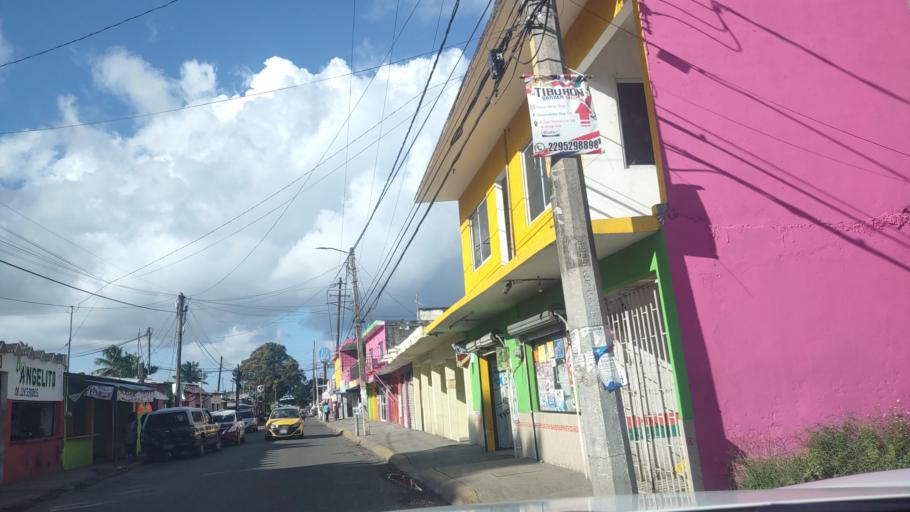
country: MX
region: Veracruz
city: El Tejar
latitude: 19.0700
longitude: -96.1614
